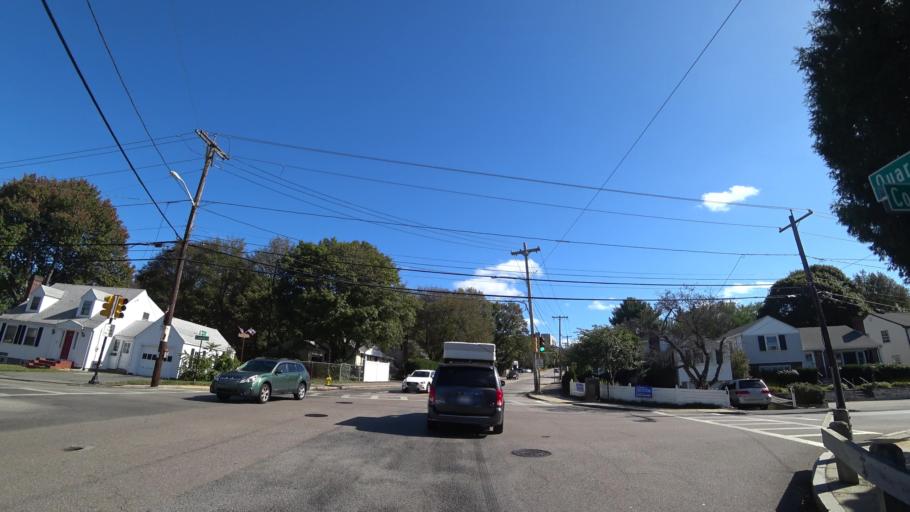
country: US
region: Massachusetts
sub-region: Norfolk County
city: Quincy
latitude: 42.2502
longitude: -71.0258
